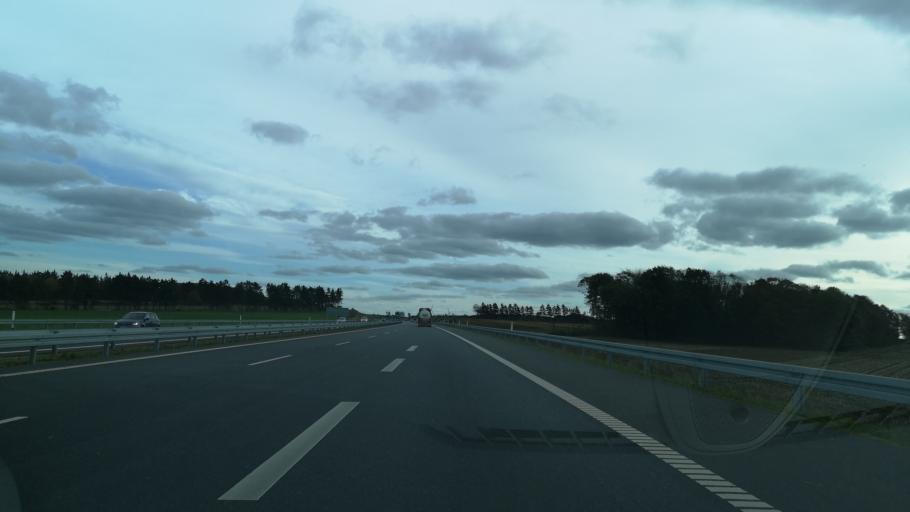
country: DK
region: Central Jutland
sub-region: Herning Kommune
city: Avlum
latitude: 56.2890
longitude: 8.7310
